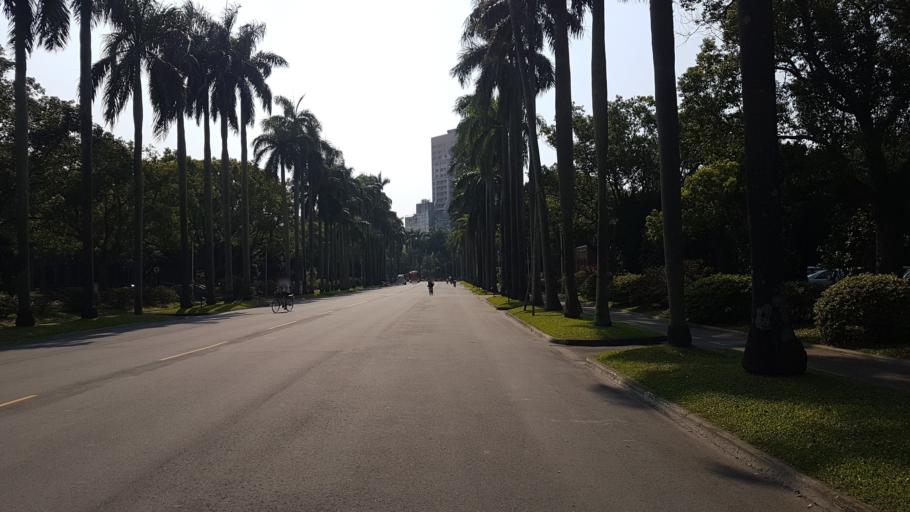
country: TW
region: Taipei
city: Taipei
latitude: 25.0174
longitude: 121.5365
